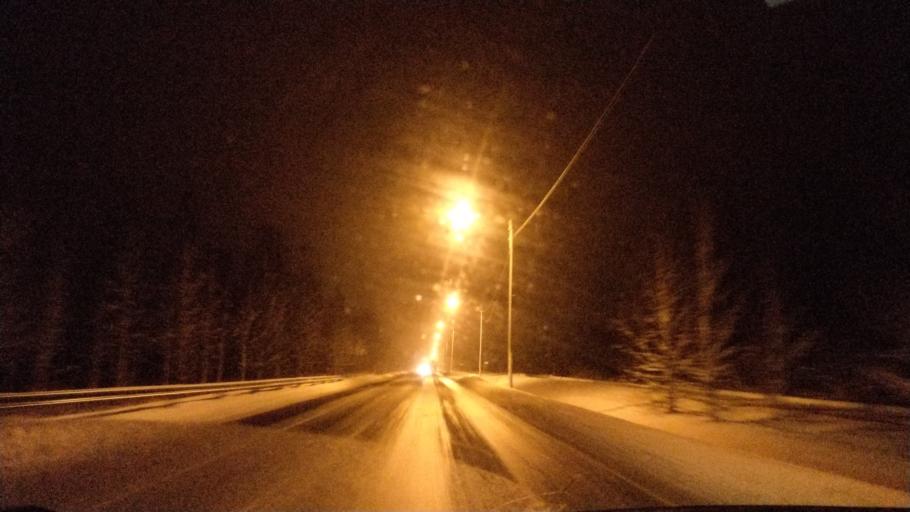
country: FI
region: Lapland
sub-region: Rovaniemi
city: Rovaniemi
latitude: 66.2840
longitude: 25.3394
